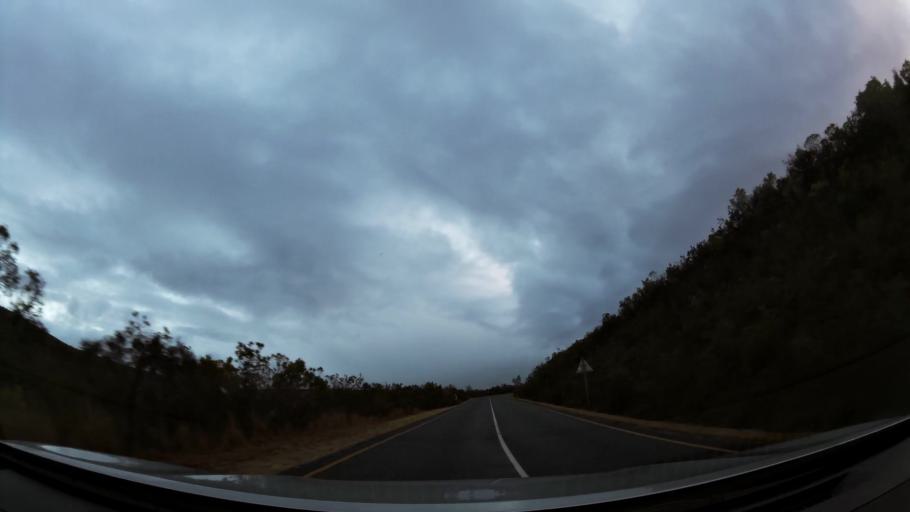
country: ZA
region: Western Cape
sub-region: Overberg District Municipality
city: Swellendam
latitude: -33.9867
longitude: 20.7171
